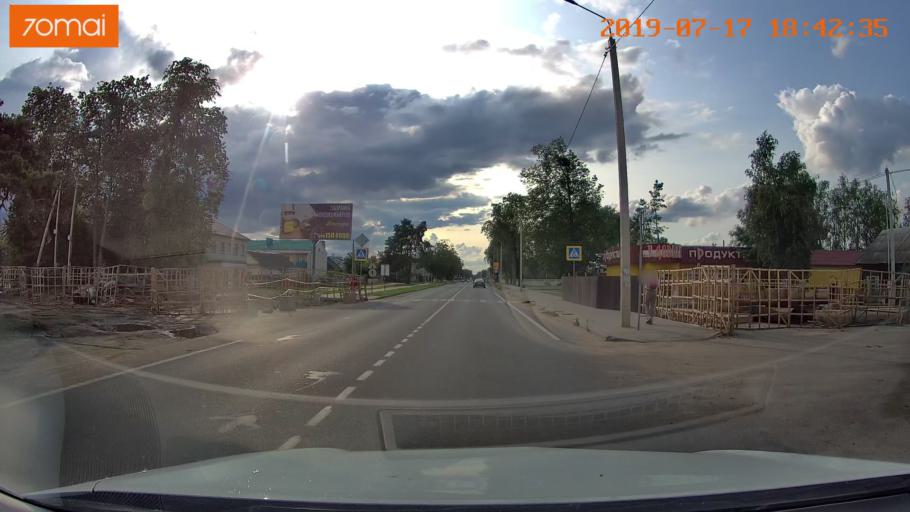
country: BY
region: Mogilev
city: Asipovichy
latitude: 53.3105
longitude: 28.6475
